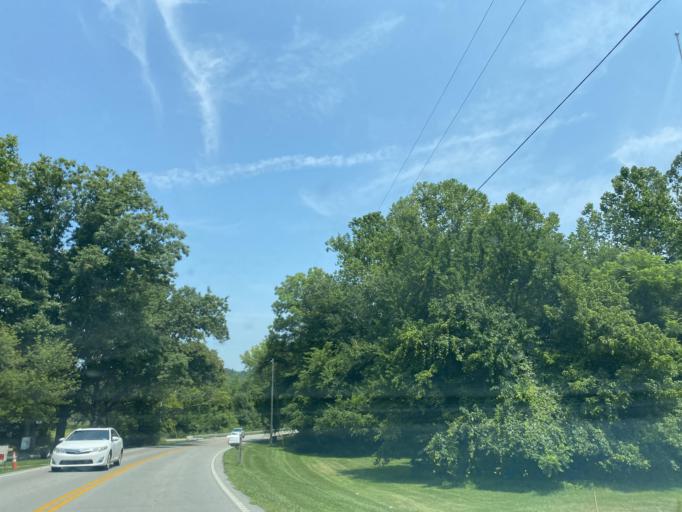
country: US
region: Kentucky
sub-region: Kenton County
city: Ryland Heights
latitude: 38.9241
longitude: -84.4398
